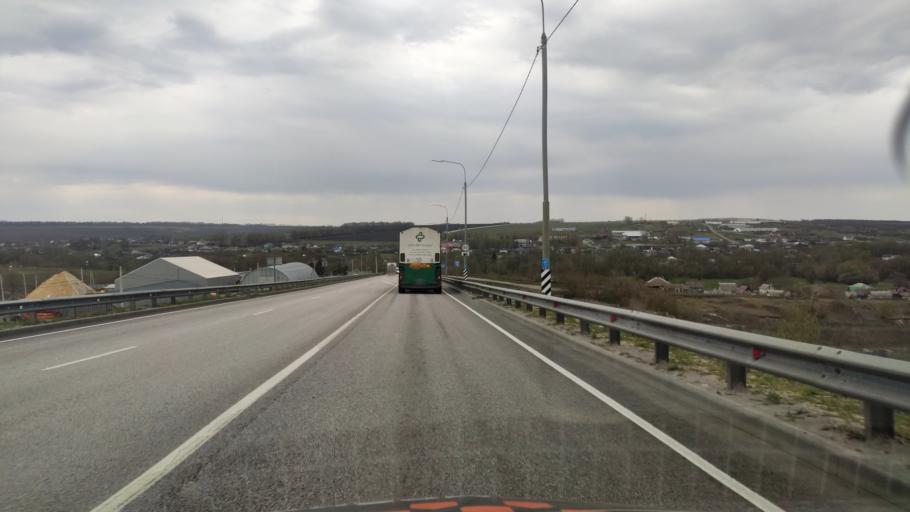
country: RU
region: Voronezj
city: Nizhnedevitsk
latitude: 51.5943
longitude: 38.5924
